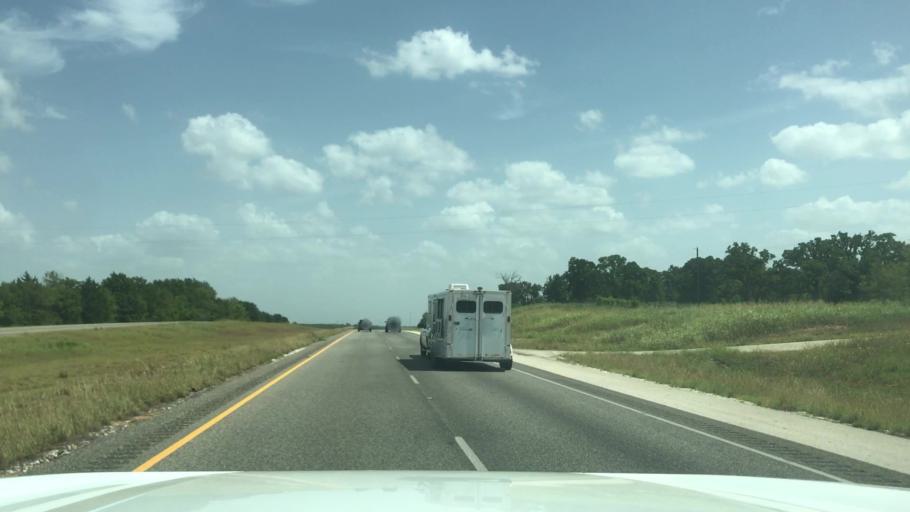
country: US
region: Texas
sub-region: Robertson County
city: Hearne
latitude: 30.9257
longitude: -96.6281
